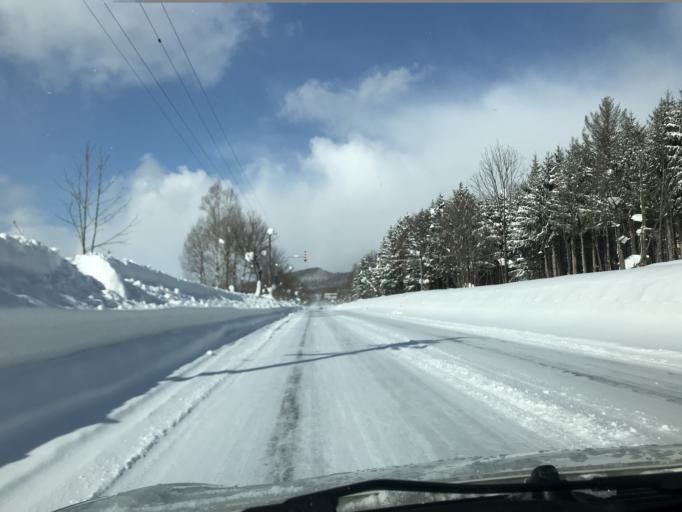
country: JP
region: Hokkaido
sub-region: Asahikawa-shi
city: Asahikawa
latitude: 43.9293
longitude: 142.4729
